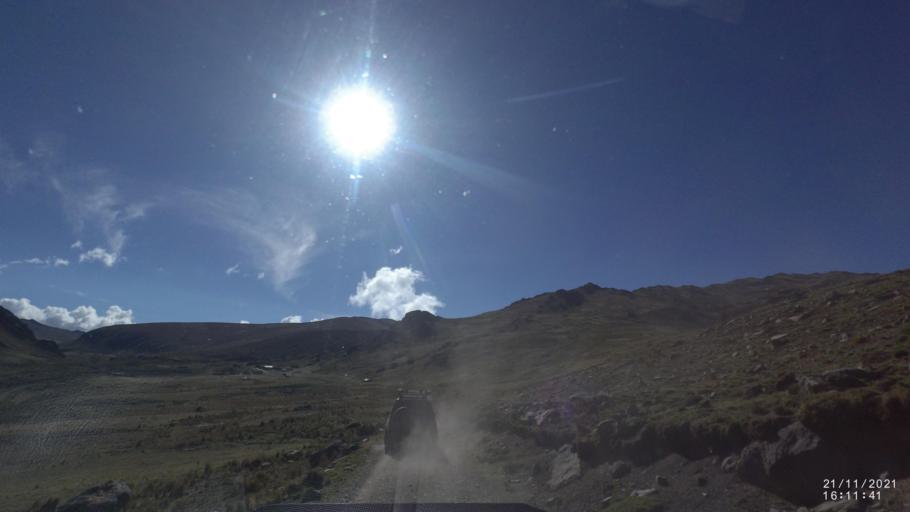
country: BO
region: Cochabamba
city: Cochabamba
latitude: -16.9956
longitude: -66.2718
